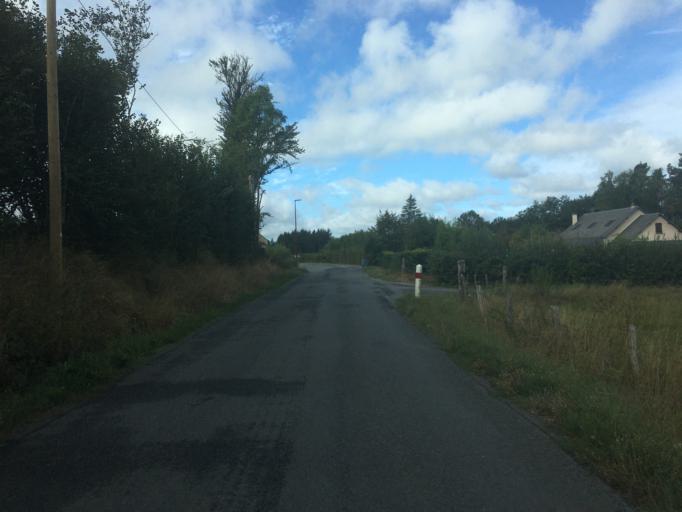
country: FR
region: Limousin
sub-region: Departement de la Correze
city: Bort-les-Orgues
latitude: 45.4174
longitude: 2.4417
